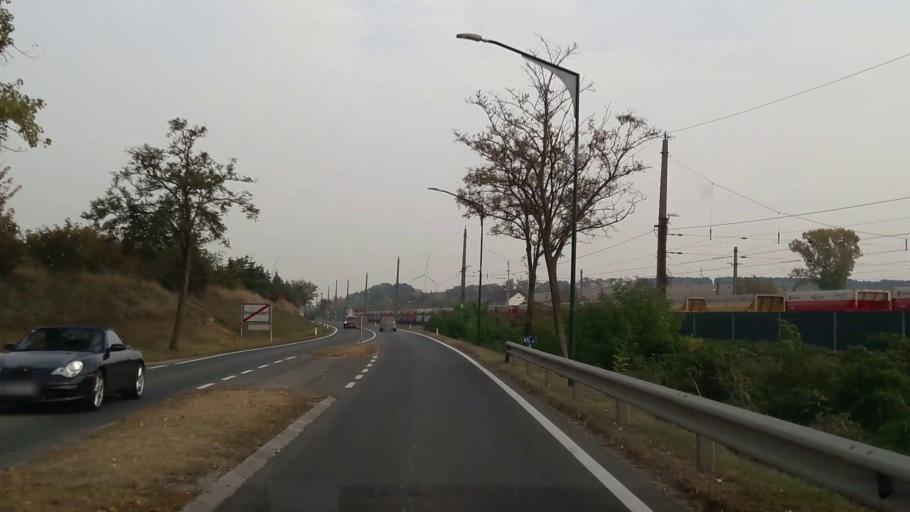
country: AT
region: Burgenland
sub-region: Politischer Bezirk Neusiedl am See
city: Bruckneudorf
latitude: 48.0180
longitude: 16.7939
